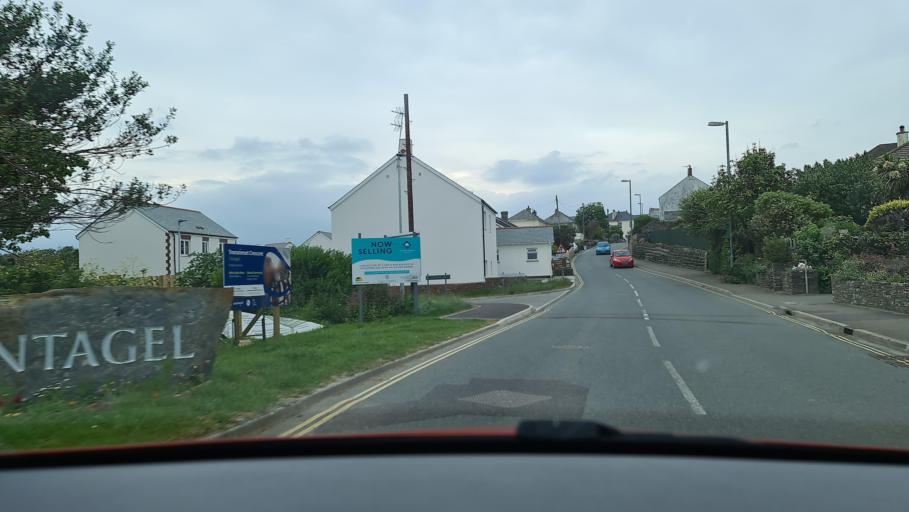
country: GB
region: England
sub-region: Cornwall
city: Tintagel
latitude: 50.6609
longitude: -4.7505
